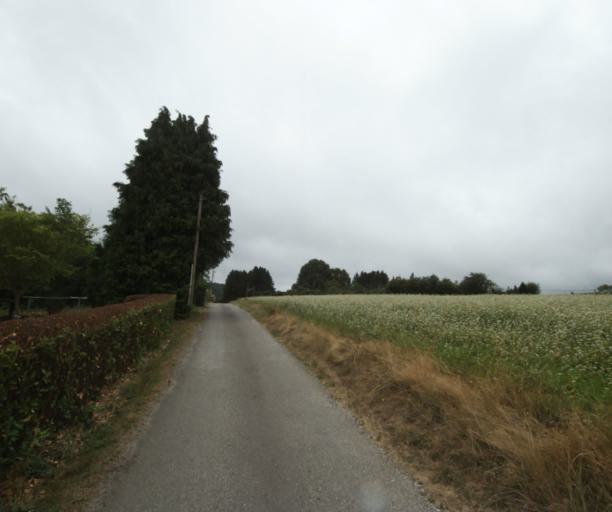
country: FR
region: Midi-Pyrenees
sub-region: Departement du Tarn
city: Soreze
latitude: 43.4039
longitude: 2.0523
